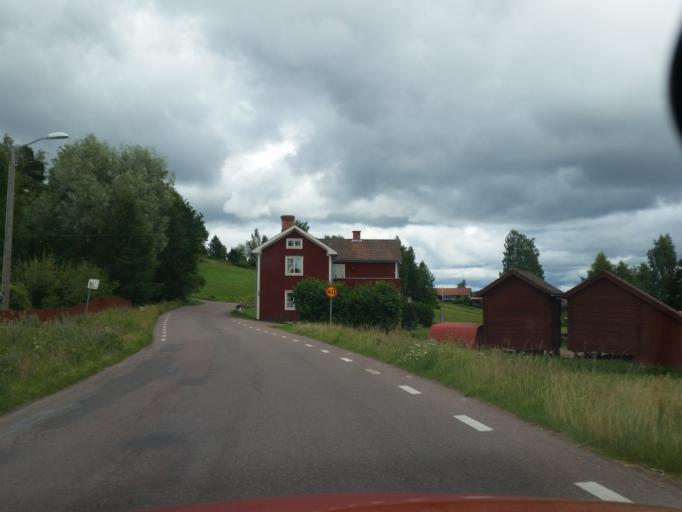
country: SE
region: Dalarna
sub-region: Leksand Municipality
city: Smedby
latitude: 60.7136
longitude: 15.0522
